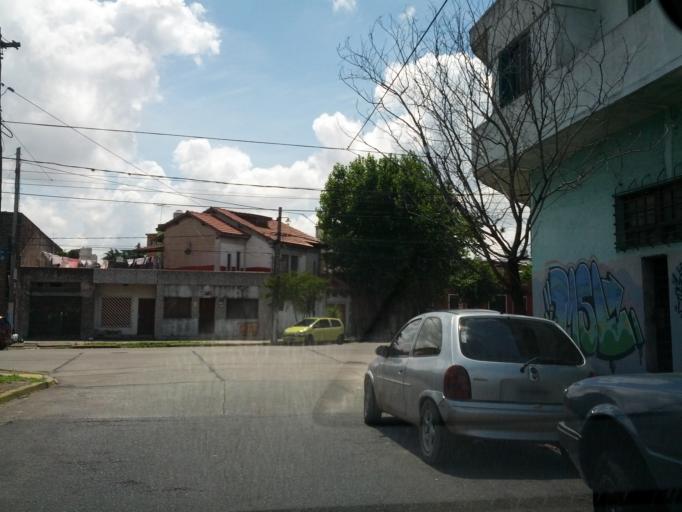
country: AR
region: Buenos Aires
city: San Justo
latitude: -34.6437
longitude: -58.5444
